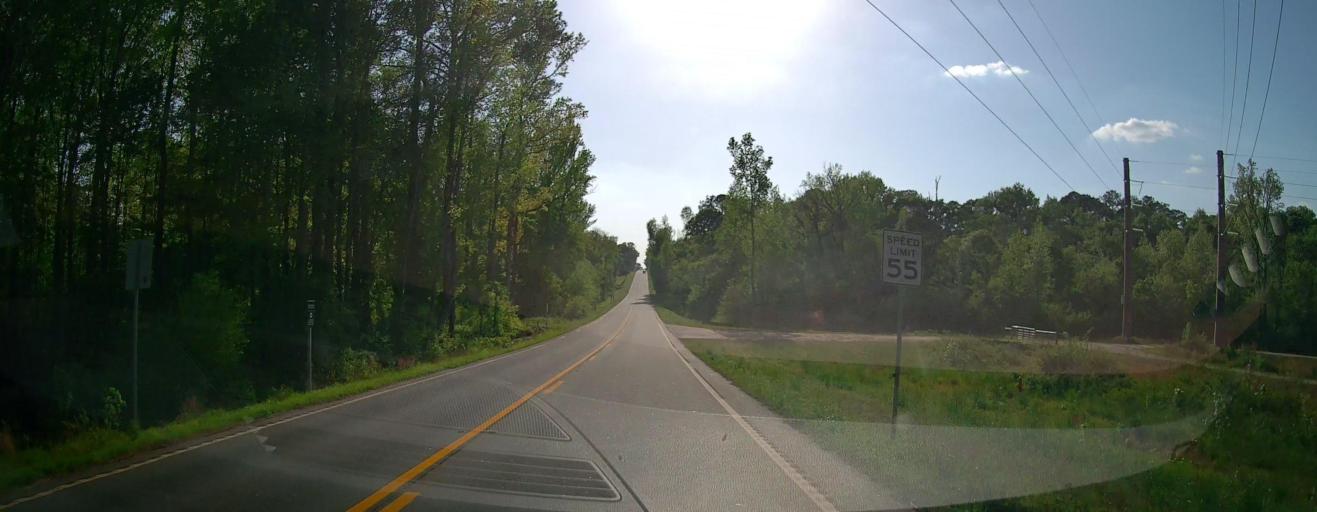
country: US
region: Georgia
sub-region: Walton County
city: Social Circle
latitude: 33.6073
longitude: -83.7068
